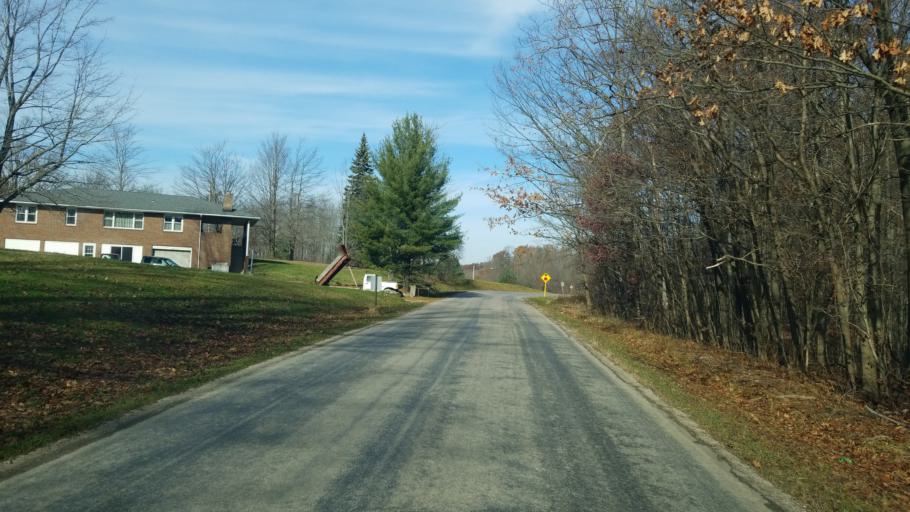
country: US
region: Ohio
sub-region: Ashtabula County
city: Geneva
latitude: 41.7490
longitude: -80.9416
